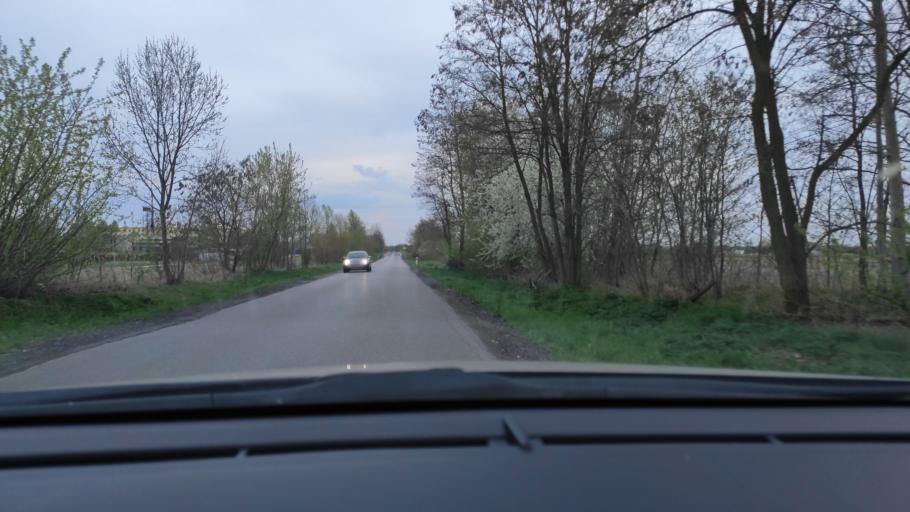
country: PL
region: Masovian Voivodeship
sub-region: Powiat zwolenski
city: Zwolen
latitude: 51.3668
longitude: 21.5641
